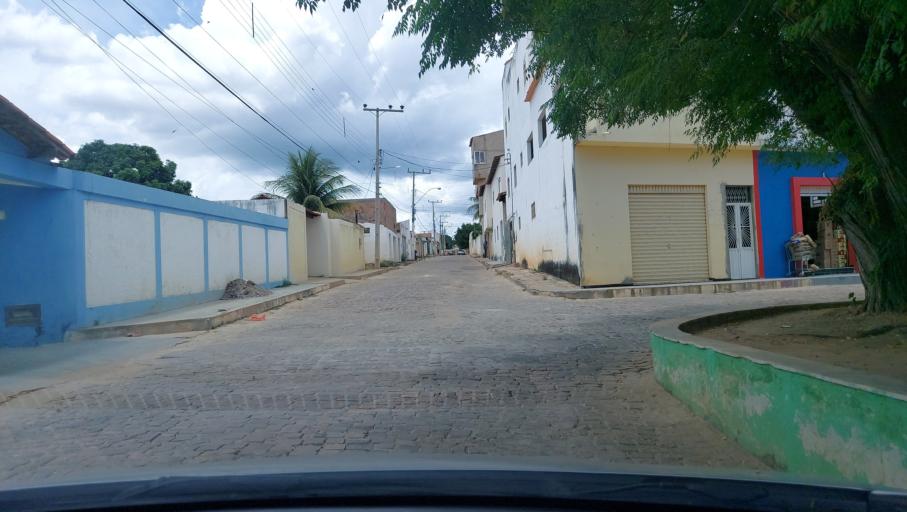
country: BR
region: Bahia
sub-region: Oliveira Dos Brejinhos
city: Beira Rio
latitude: -12.0028
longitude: -42.6264
